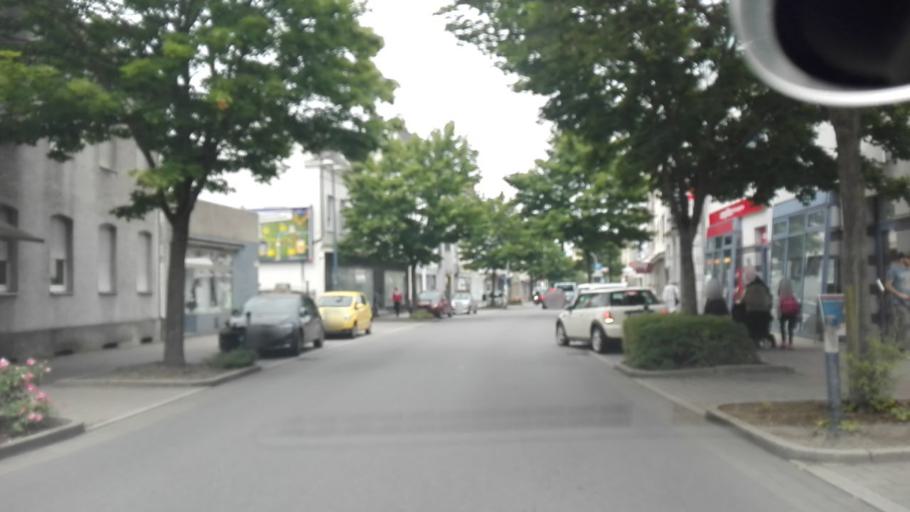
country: DE
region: North Rhine-Westphalia
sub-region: Regierungsbezirk Arnsberg
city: Holzwickede
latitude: 51.5010
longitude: 7.6160
